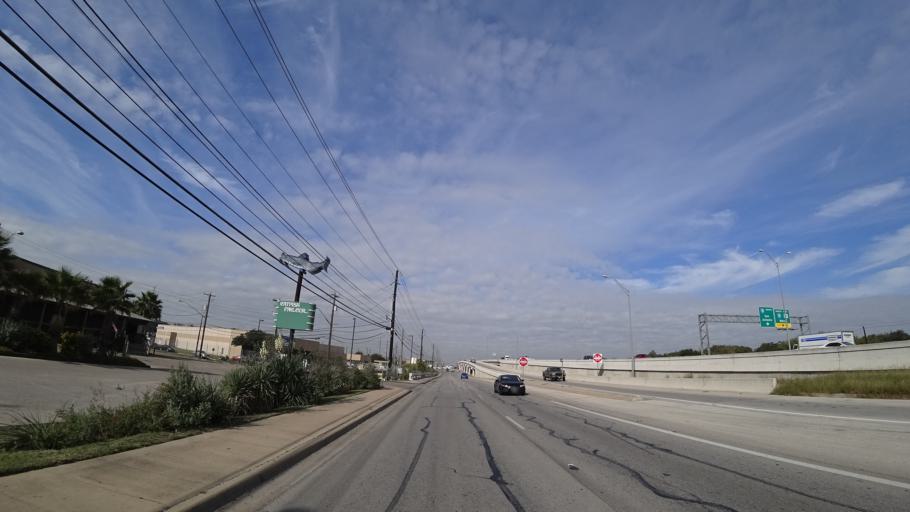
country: US
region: Texas
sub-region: Travis County
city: Austin
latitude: 30.2142
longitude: -97.7311
